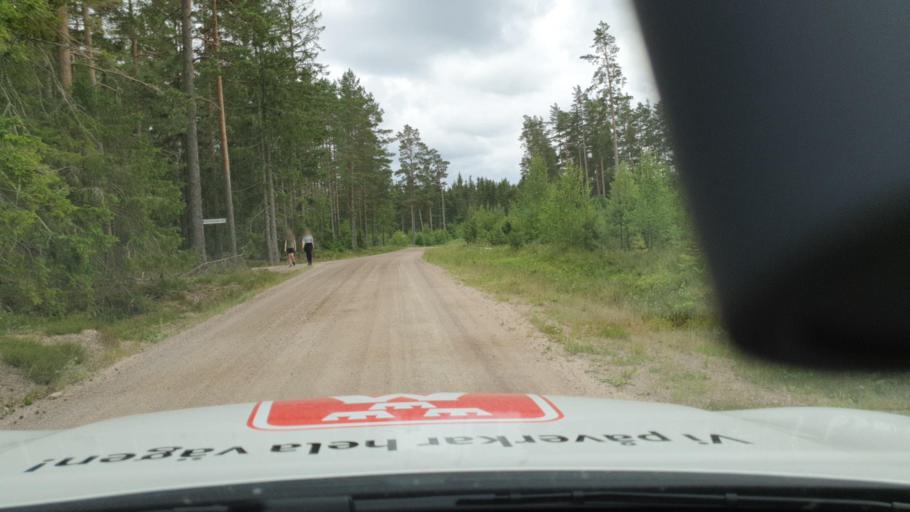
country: SE
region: Vaestra Goetaland
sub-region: Tidaholms Kommun
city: Olofstorp
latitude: 58.2032
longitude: 14.1098
